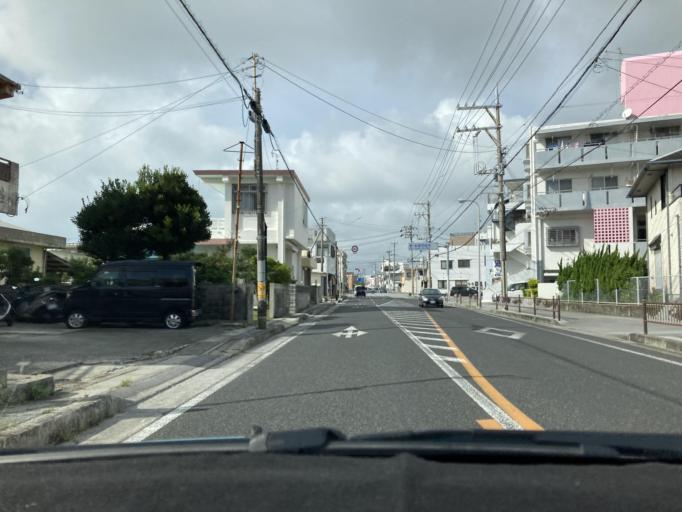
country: JP
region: Okinawa
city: Itoman
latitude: 26.1246
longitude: 127.6697
